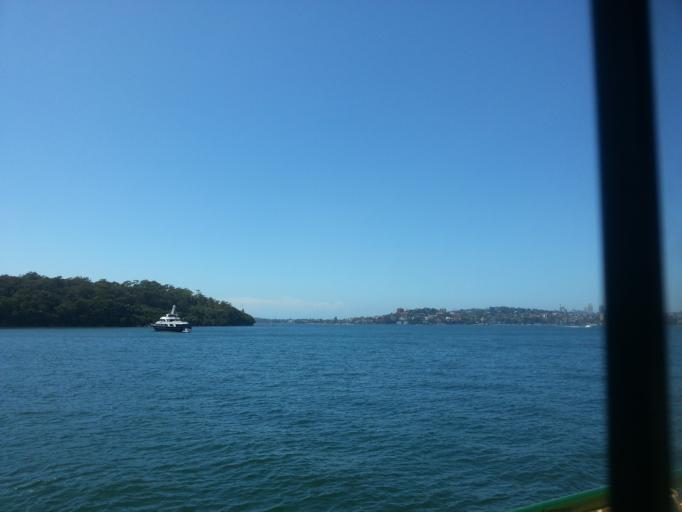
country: AU
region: New South Wales
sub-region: Mosman
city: Mosman
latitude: -33.8477
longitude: 151.2391
